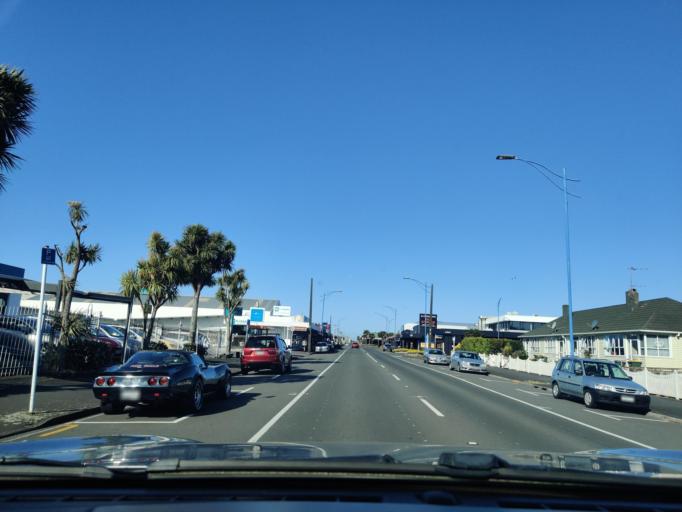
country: NZ
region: Taranaki
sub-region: New Plymouth District
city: New Plymouth
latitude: -39.0498
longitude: 174.1004
